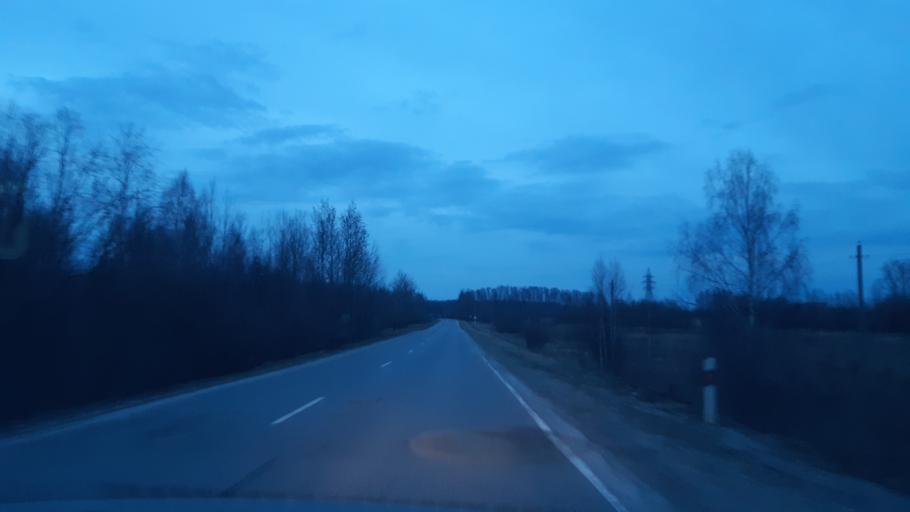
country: RU
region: Vladimir
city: Luknovo
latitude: 56.2176
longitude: 42.0316
